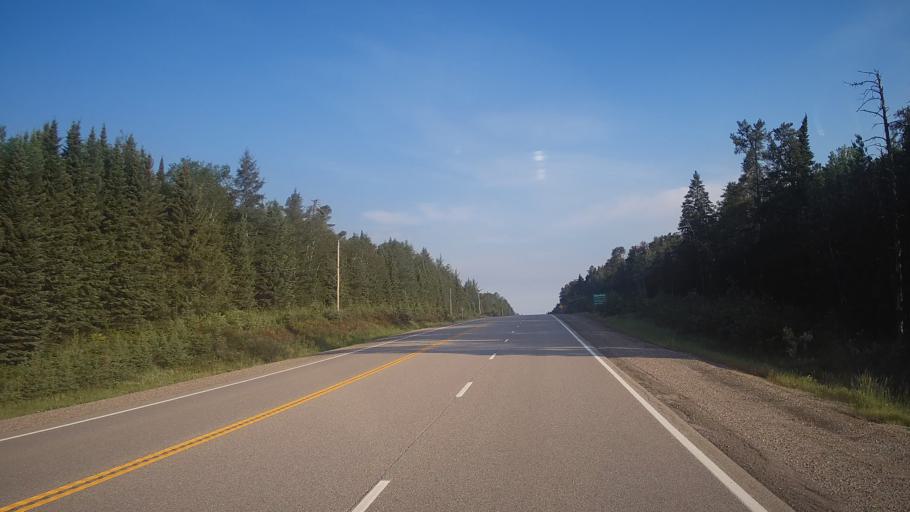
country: CA
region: Ontario
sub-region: Rainy River District
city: Atikokan
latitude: 49.3742
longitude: -91.5751
